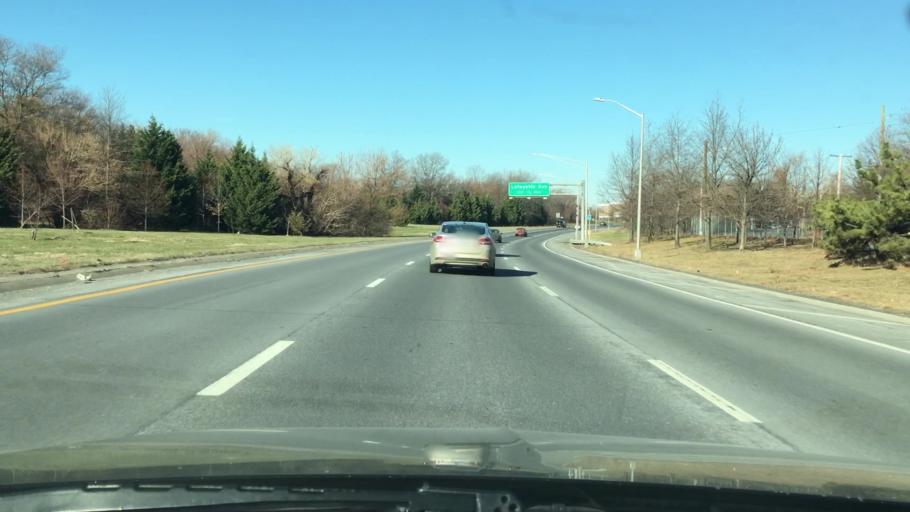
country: US
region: New York
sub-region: Bronx
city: The Bronx
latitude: 40.8213
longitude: -73.8136
